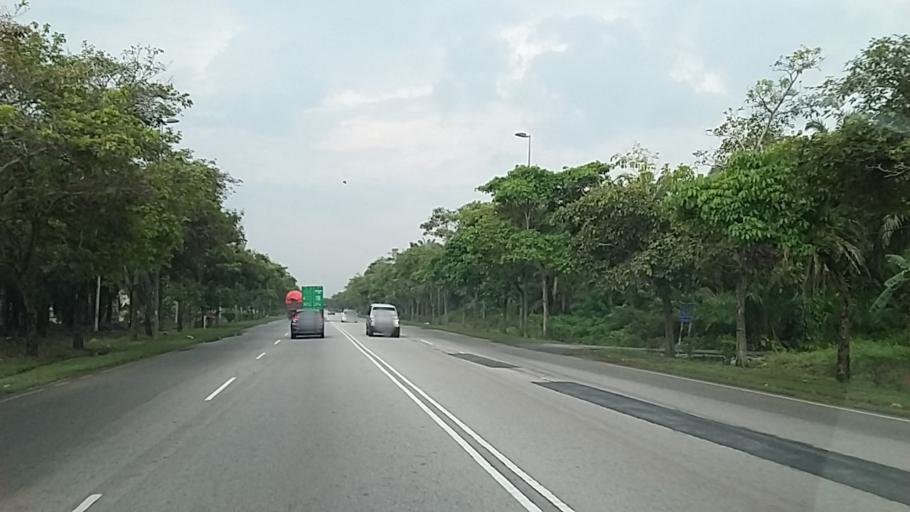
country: MY
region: Johor
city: Parit Raja
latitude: 1.8729
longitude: 103.1346
